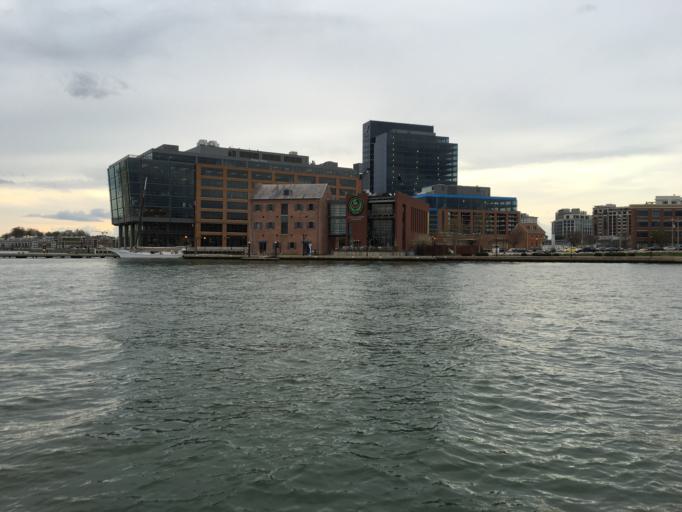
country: US
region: Maryland
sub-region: City of Baltimore
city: Baltimore
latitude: 39.2786
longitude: -76.5946
